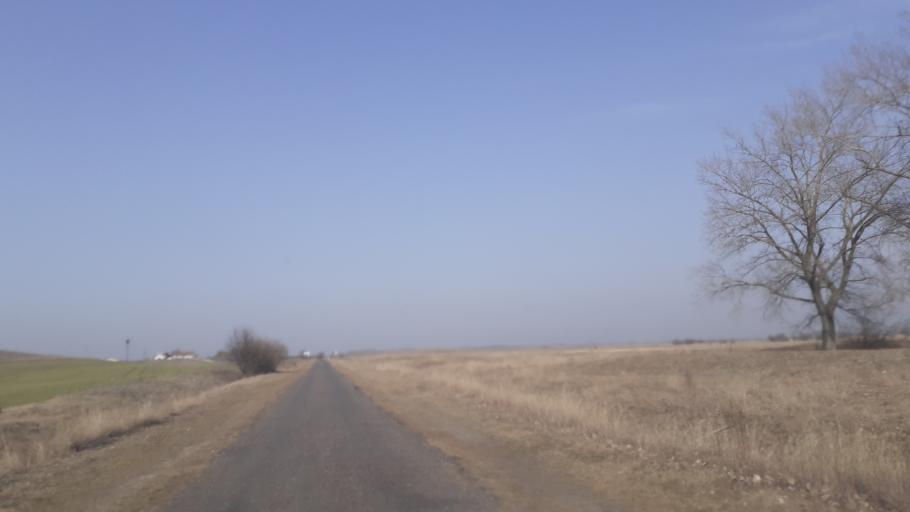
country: HU
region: Pest
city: Dabas
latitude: 47.0913
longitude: 19.2349
